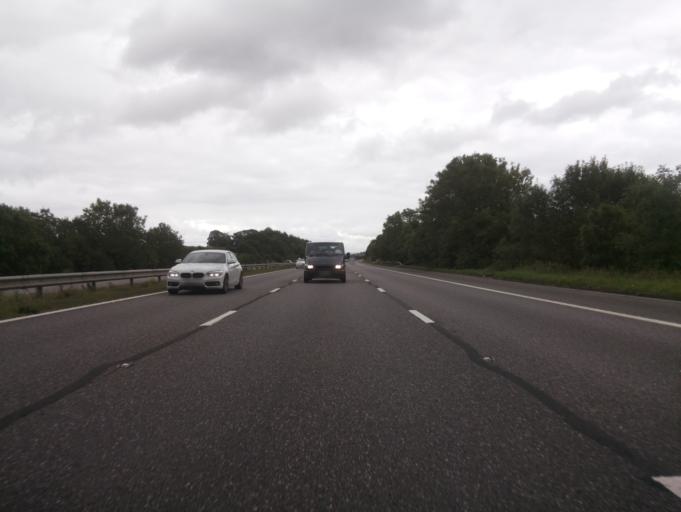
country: GB
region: England
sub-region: Devon
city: Uffculme
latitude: 50.9534
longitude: -3.2597
